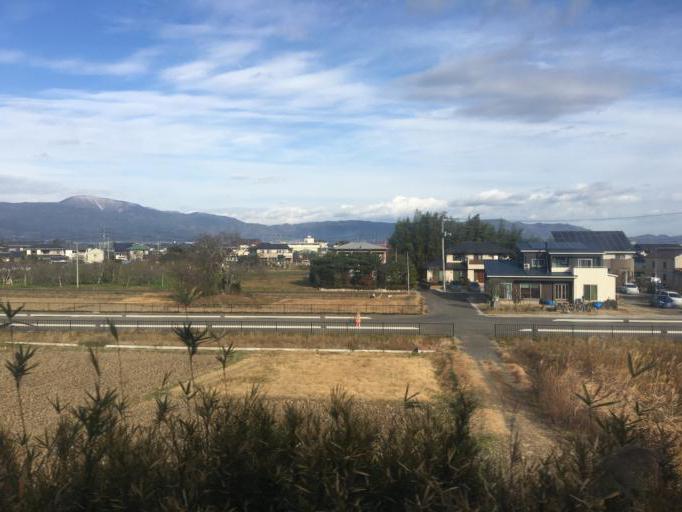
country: JP
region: Fukushima
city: Hobaramachi
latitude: 37.8096
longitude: 140.5409
